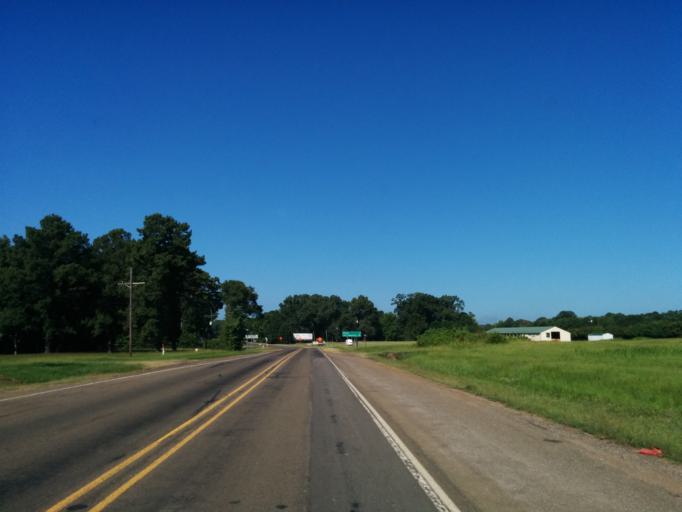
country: US
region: Texas
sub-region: Sabine County
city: Milam
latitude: 31.4609
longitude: -93.7560
